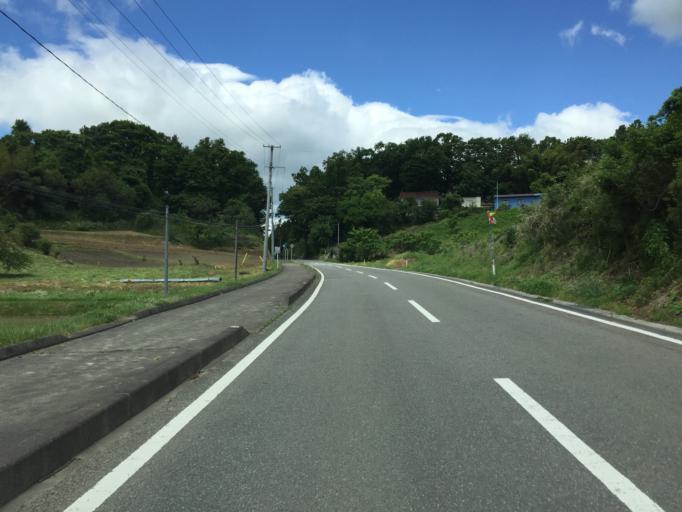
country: JP
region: Fukushima
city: Nihommatsu
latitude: 37.5540
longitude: 140.4675
